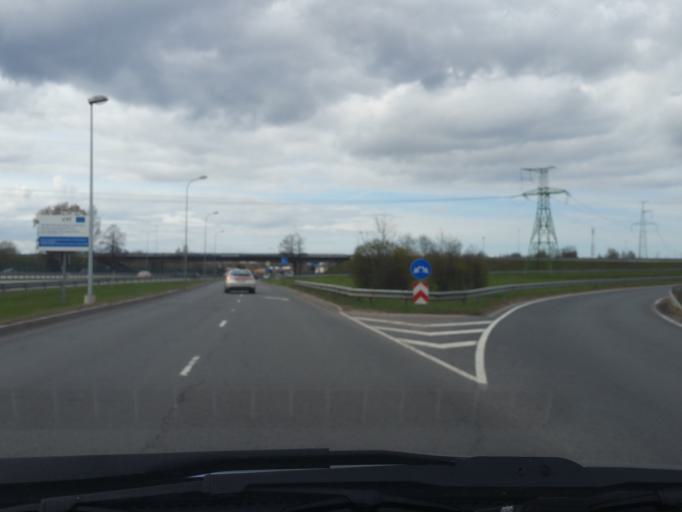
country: LV
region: Marupe
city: Marupe
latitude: 56.9304
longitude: 24.0128
